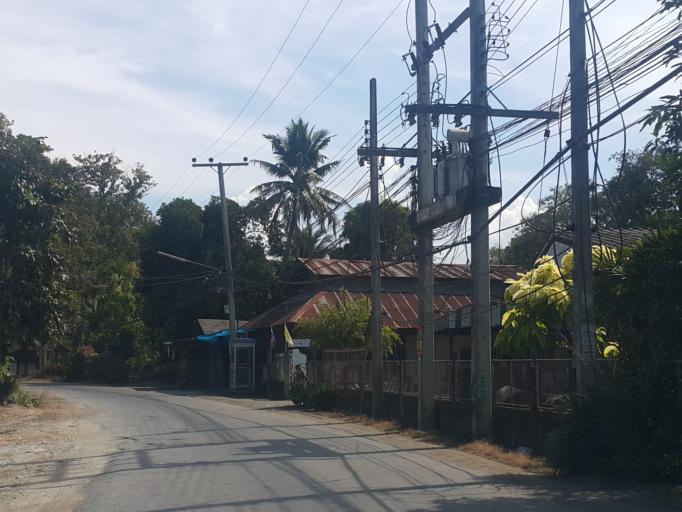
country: TH
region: Chiang Mai
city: Mae On
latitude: 18.8210
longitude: 99.1743
